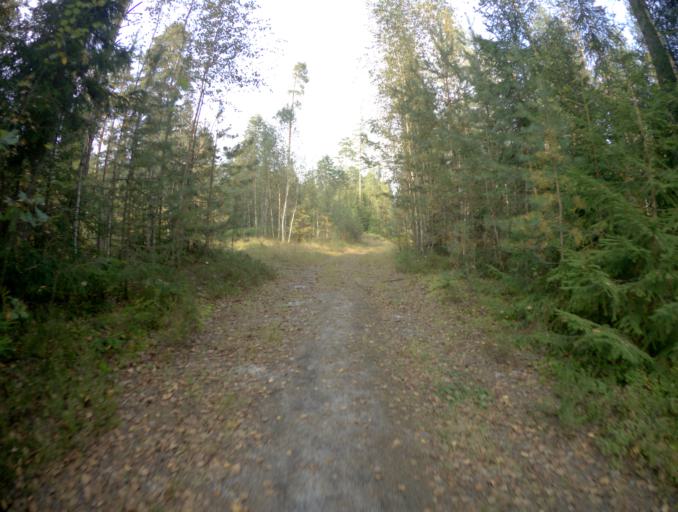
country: RU
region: Vladimir
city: Bogolyubovo
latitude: 56.0949
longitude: 40.5456
